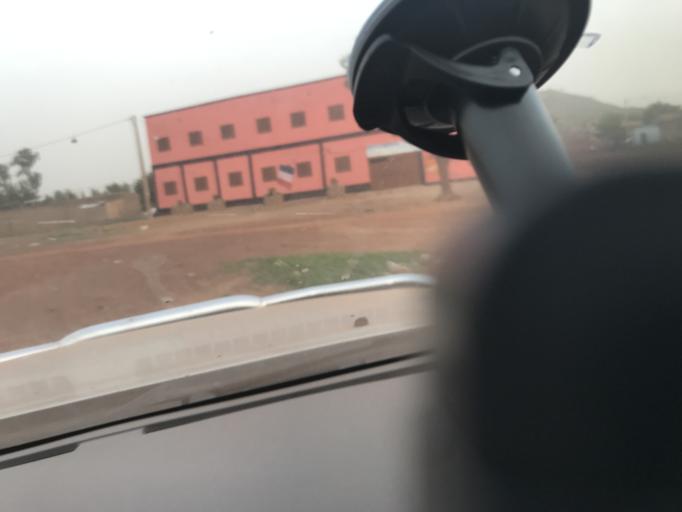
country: ML
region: Bamako
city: Bamako
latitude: 12.6530
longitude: -7.8875
